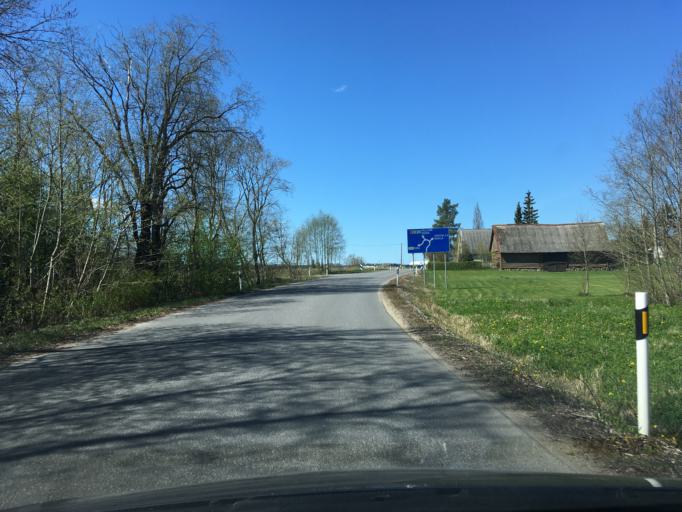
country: EE
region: Harju
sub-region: Rae vald
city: Vaida
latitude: 59.1977
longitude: 25.0495
